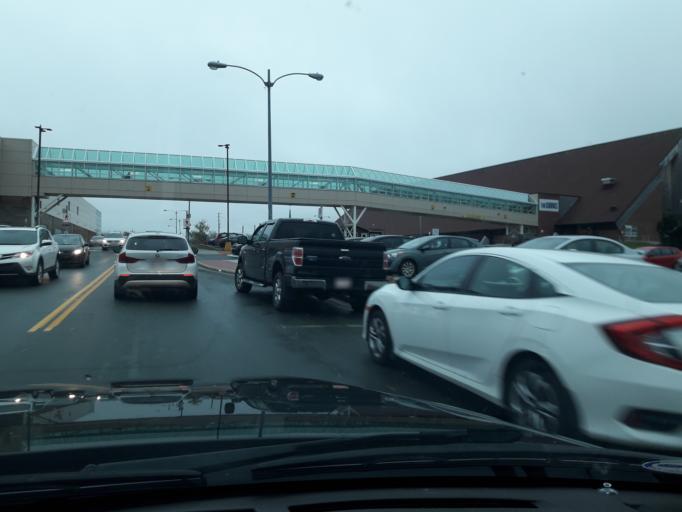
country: CA
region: Newfoundland and Labrador
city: St. John's
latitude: 47.5704
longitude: -52.7363
